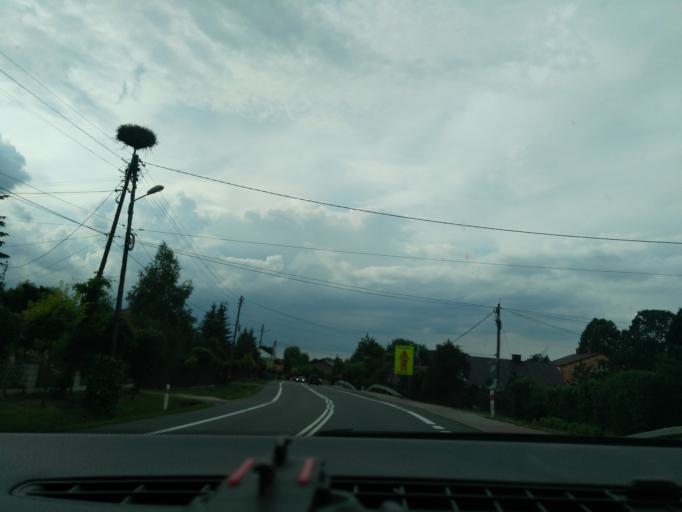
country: PL
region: Subcarpathian Voivodeship
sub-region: Powiat rzeszowski
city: Kamien
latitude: 50.3319
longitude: 22.1372
